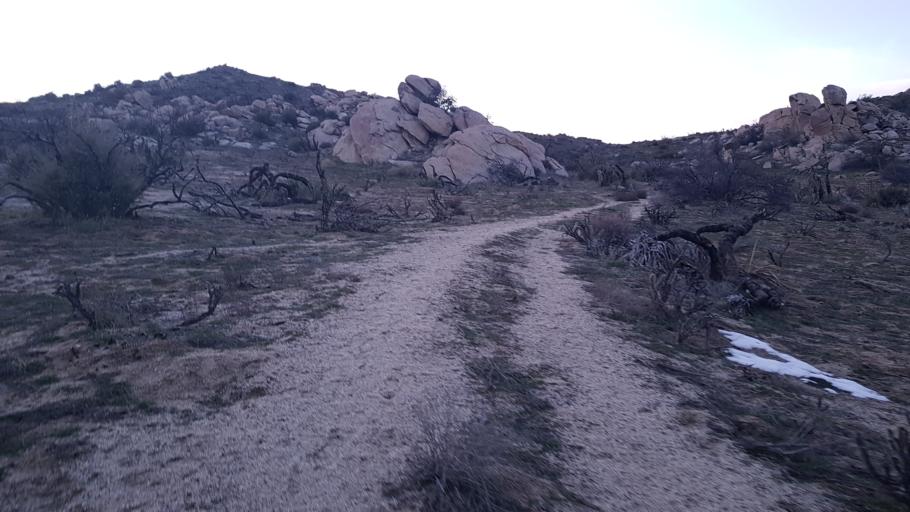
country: US
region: California
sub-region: San Diego County
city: Borrego Springs
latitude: 33.1801
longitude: -116.4487
